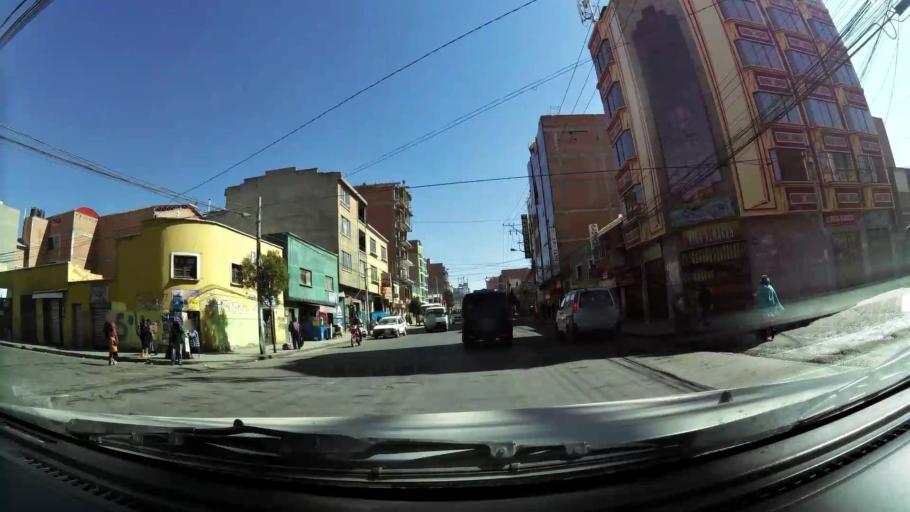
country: BO
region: La Paz
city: La Paz
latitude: -16.5121
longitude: -68.1577
